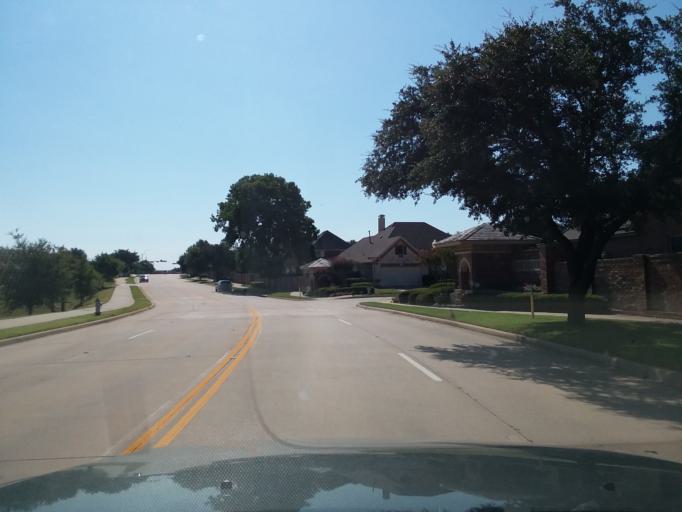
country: US
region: Texas
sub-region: Denton County
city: Flower Mound
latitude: 33.0335
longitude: -97.0739
